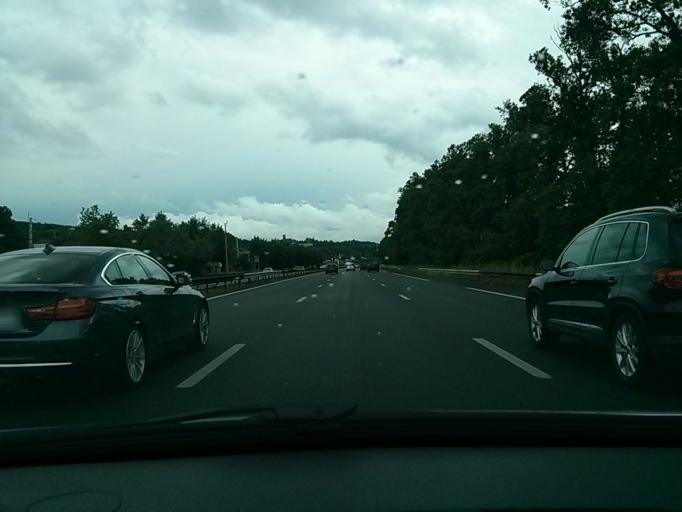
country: FR
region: Rhone-Alpes
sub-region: Departement du Rhone
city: Serezin-du-Rhone
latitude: 45.6228
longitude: 4.8141
